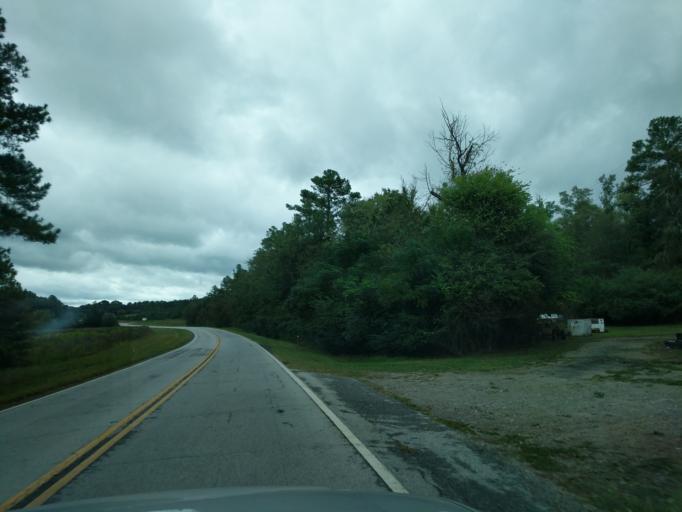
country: US
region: Georgia
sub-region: Elbert County
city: Elberton
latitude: 34.0223
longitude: -82.7909
